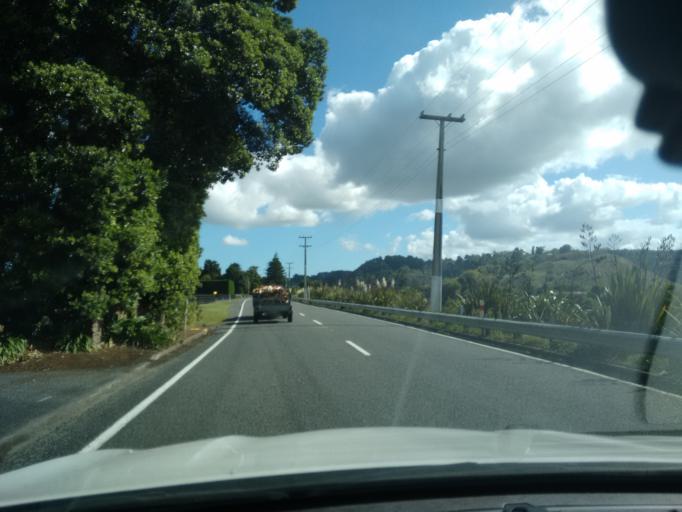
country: NZ
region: Manawatu-Wanganui
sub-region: Wanganui District
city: Wanganui
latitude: -39.8971
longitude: 175.0864
